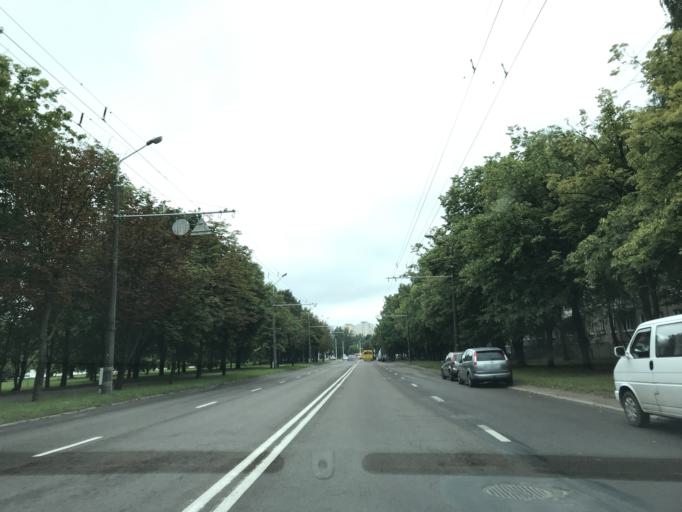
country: BY
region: Minsk
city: Borovlyany
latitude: 53.9462
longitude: 27.6417
